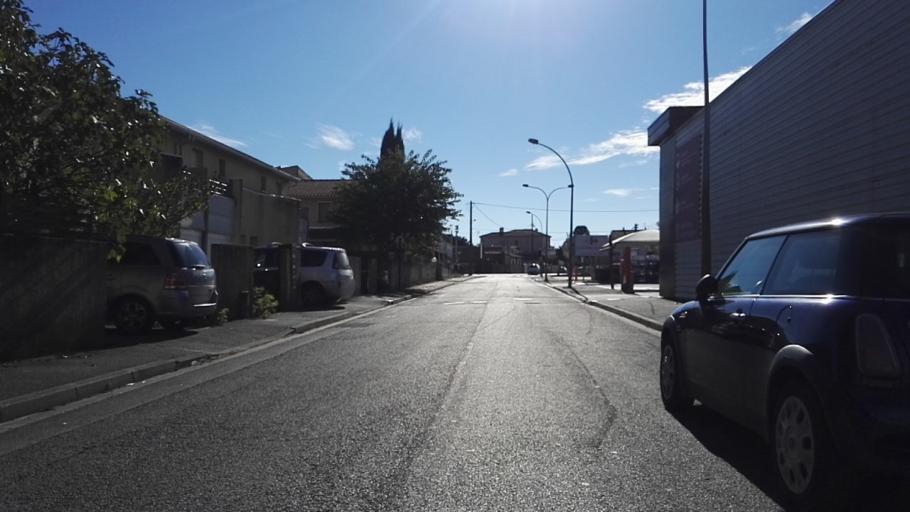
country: FR
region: Aquitaine
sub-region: Departement de la Gironde
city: Eysines
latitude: 44.8611
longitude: -0.6337
